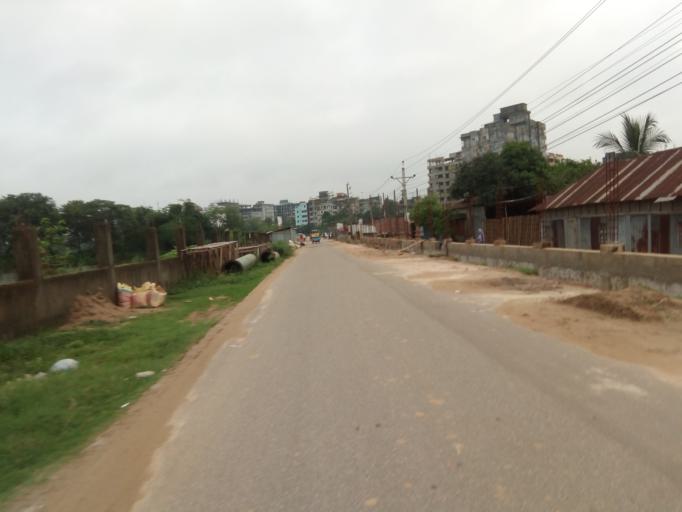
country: BD
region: Dhaka
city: Tungi
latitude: 23.8486
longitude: 90.4169
